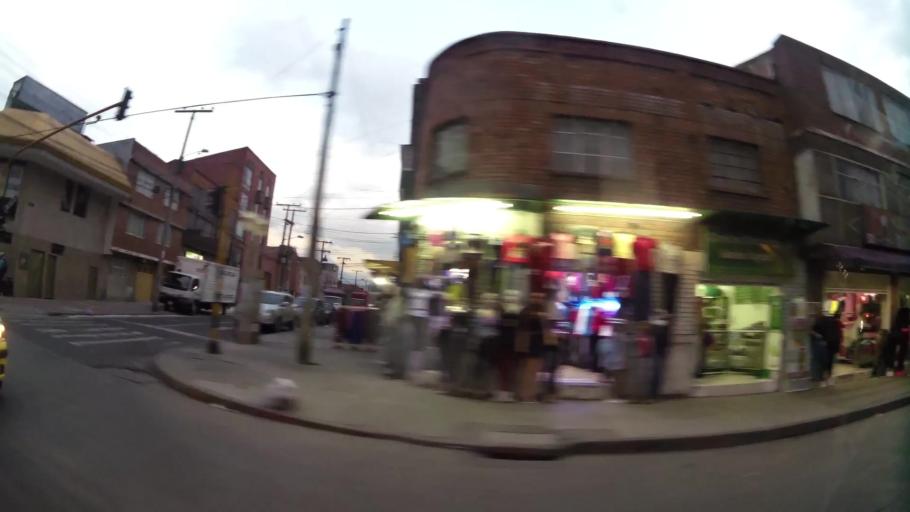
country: CO
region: Bogota D.C.
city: Bogota
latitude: 4.5836
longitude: -74.1257
